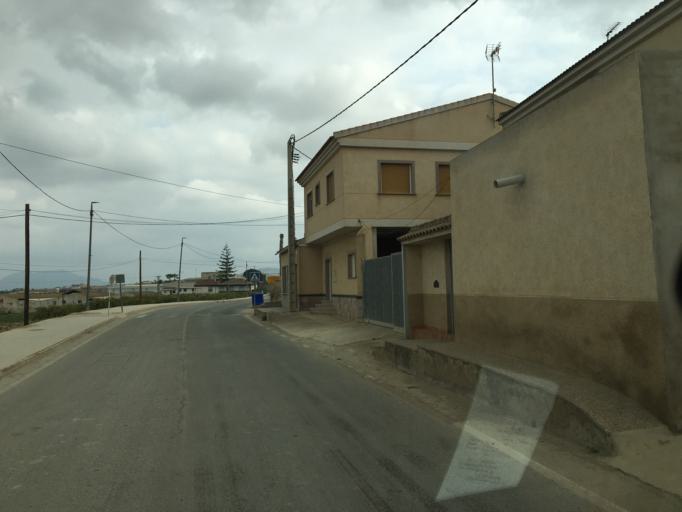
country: ES
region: Murcia
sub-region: Murcia
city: Beniel
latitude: 38.0151
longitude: -0.9896
